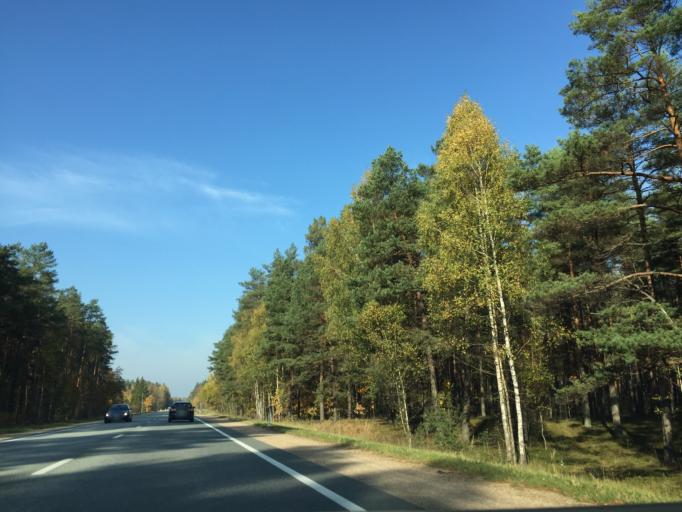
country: LV
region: Babite
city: Pinki
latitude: 56.8899
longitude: 23.9377
